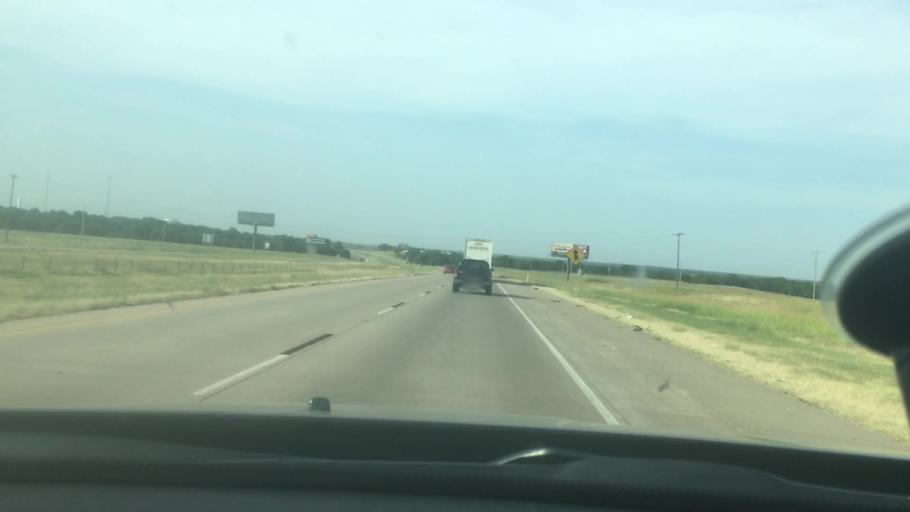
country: US
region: Oklahoma
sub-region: Carter County
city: Ardmore
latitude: 34.3319
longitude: -97.1531
